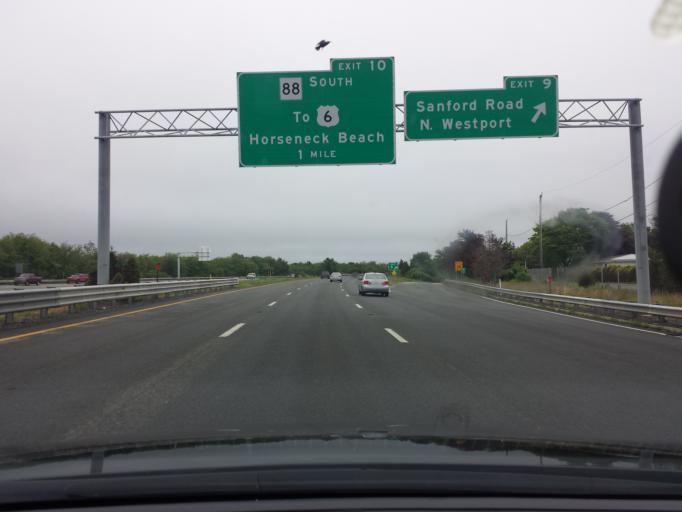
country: US
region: Massachusetts
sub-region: Bristol County
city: North Westport
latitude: 41.6802
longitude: -71.1114
